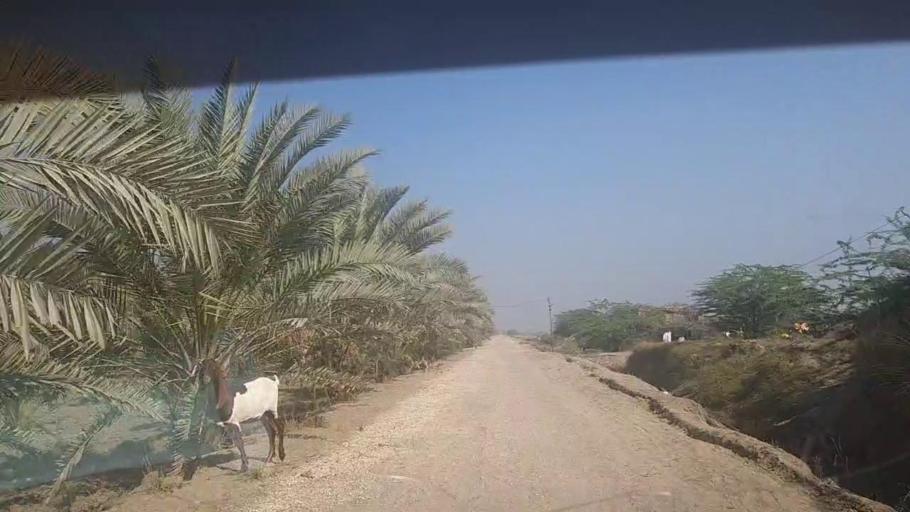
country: PK
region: Sindh
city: Khairpur
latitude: 27.4607
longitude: 68.7290
